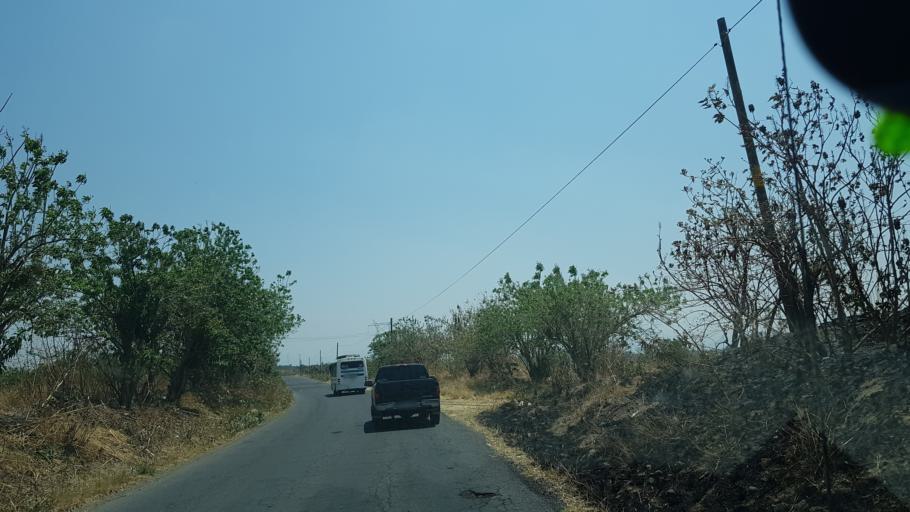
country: MX
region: Puebla
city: Tochimilco
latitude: 18.8889
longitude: -98.5284
